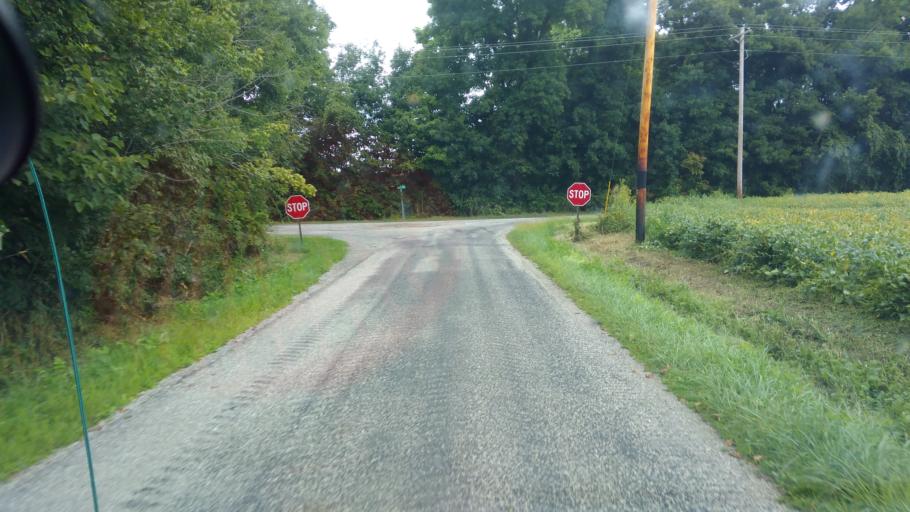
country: US
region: Ohio
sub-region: Richland County
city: Lincoln Heights
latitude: 40.8383
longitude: -82.4157
